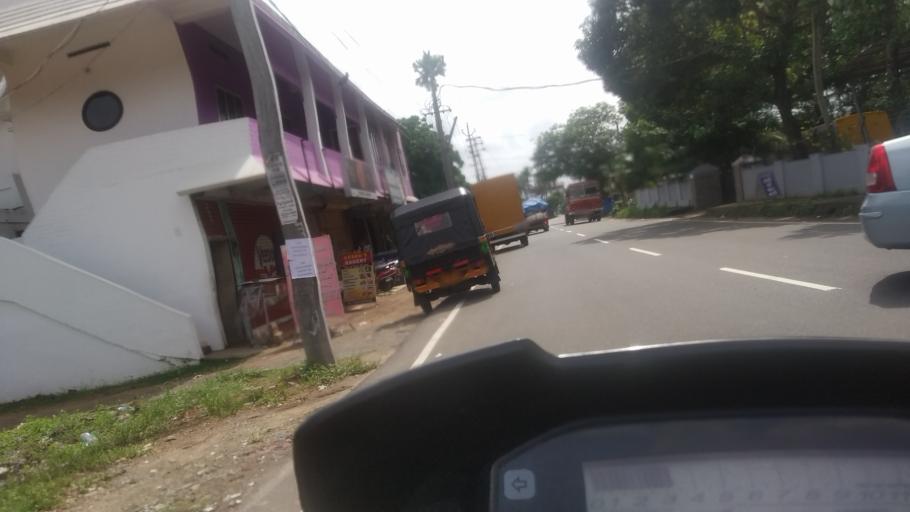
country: IN
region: Kerala
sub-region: Ernakulam
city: Aluva
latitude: 10.1260
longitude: 76.3161
